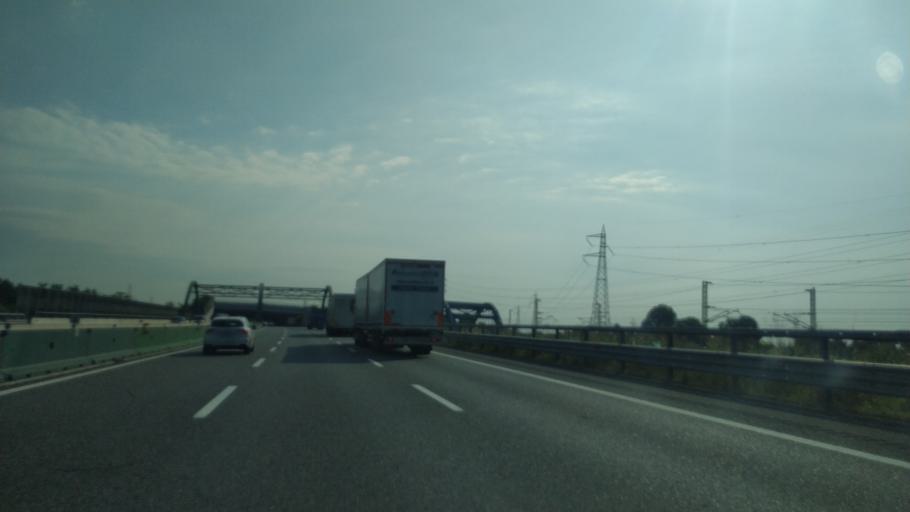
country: IT
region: Lombardy
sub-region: Citta metropolitana di Milano
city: Bernate Ticino
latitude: 45.4724
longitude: 8.8216
